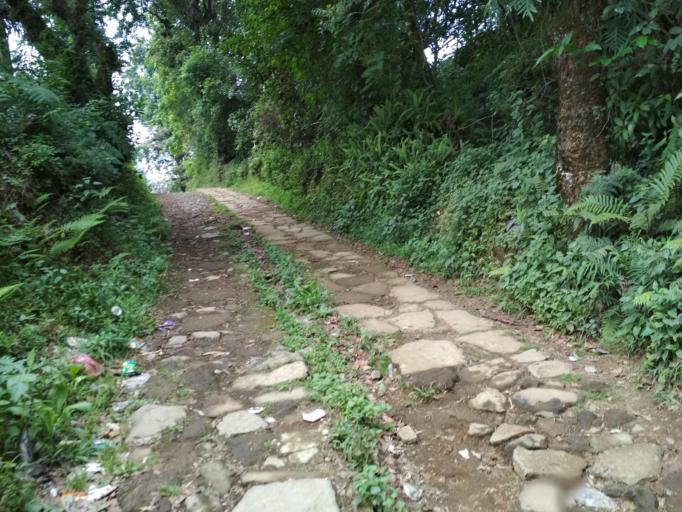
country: MX
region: Veracruz
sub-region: La Perla
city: La Perla
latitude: 18.9248
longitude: -97.1312
